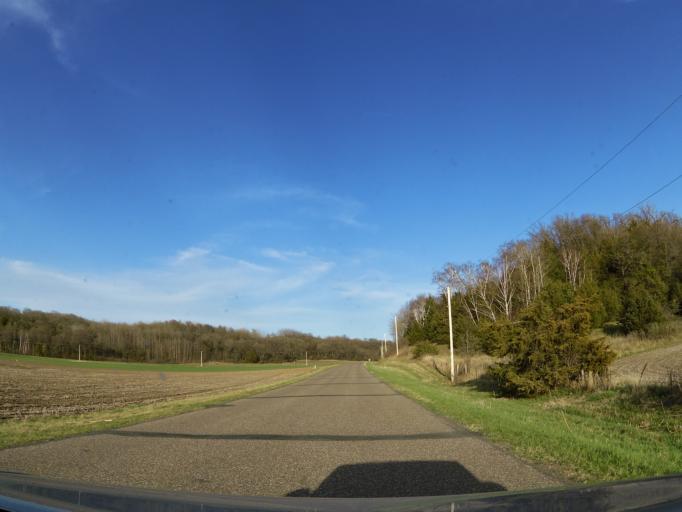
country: US
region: Wisconsin
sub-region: Pierce County
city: River Falls
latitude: 44.8870
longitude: -92.6714
